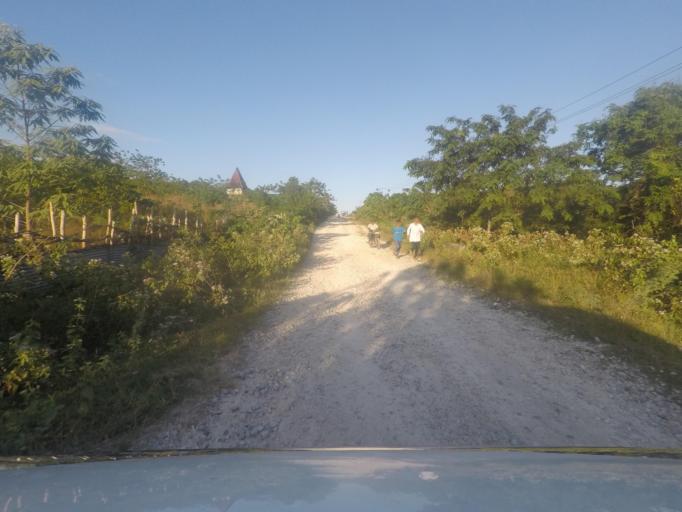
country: TL
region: Lautem
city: Lospalos
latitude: -8.3990
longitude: 127.2008
